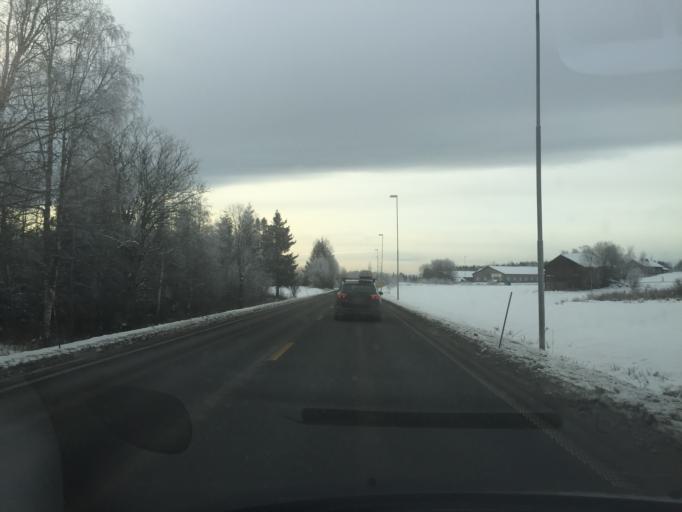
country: NO
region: Hedmark
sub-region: Elverum
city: Elverum
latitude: 60.9285
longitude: 11.6705
